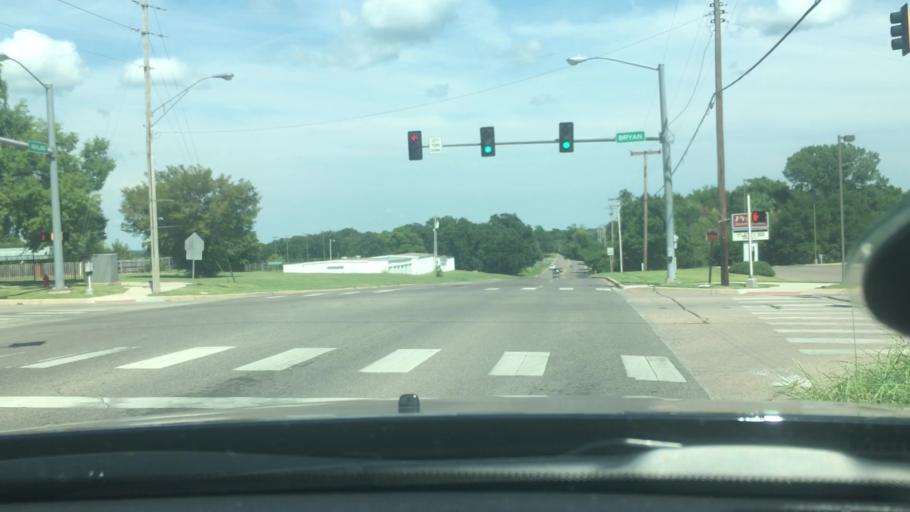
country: US
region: Oklahoma
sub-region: Pottawatomie County
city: Shawnee
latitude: 35.3326
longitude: -96.8947
